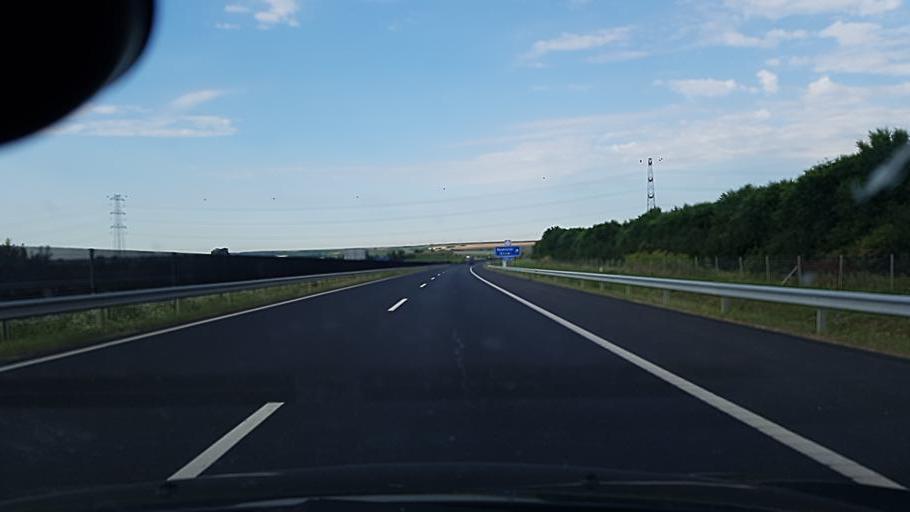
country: HU
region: Fejer
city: Rackeresztur
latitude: 47.2708
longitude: 18.8583
